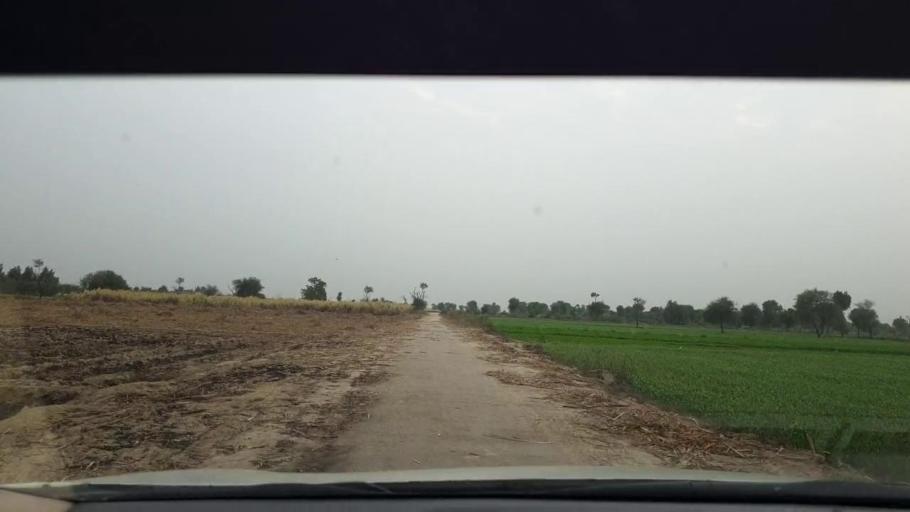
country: PK
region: Sindh
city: Jhol
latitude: 25.9268
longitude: 68.8534
